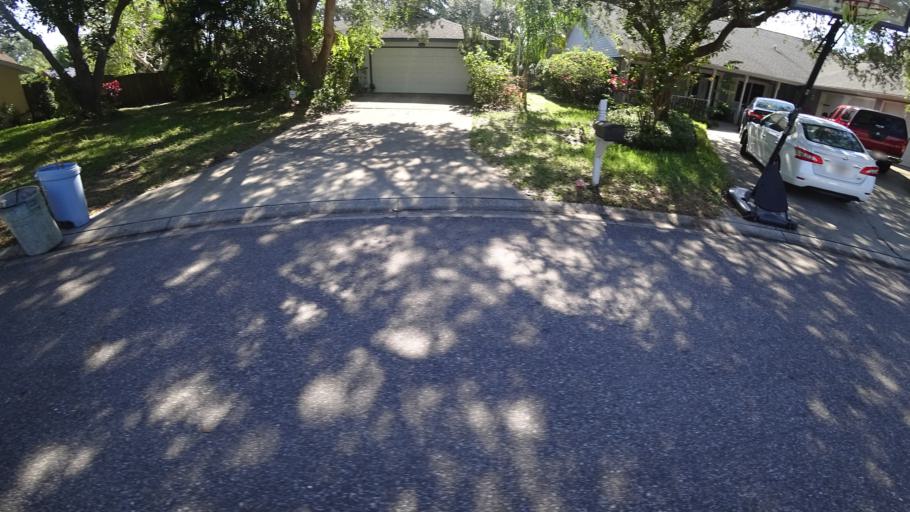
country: US
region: Florida
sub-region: Manatee County
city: West Bradenton
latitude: 27.5089
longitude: -82.6464
